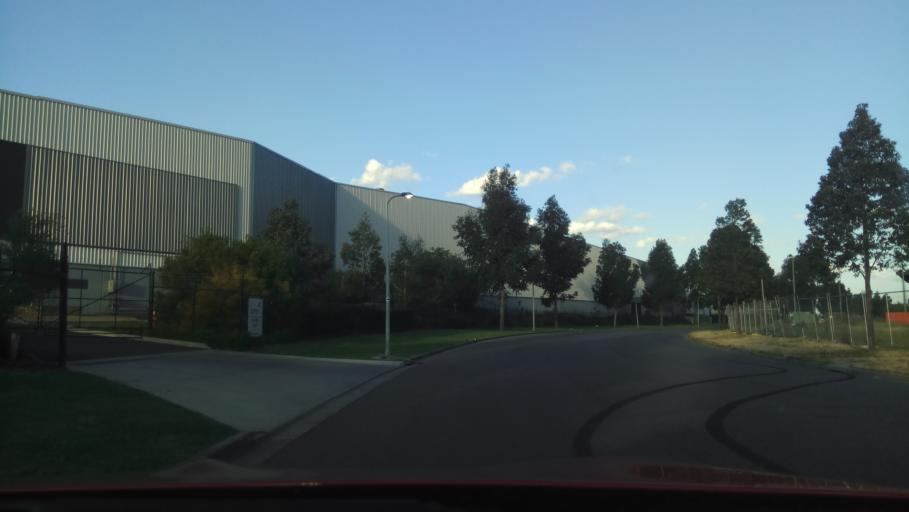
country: AU
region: Victoria
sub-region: Hobsons Bay
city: Altona
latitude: -37.8528
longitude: 144.8300
